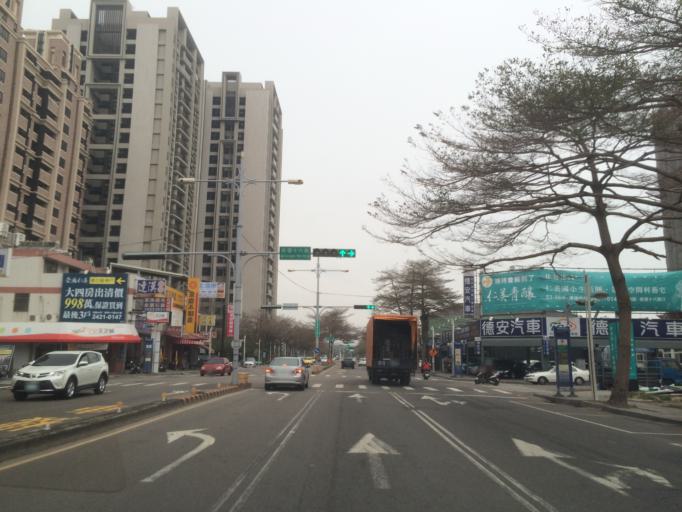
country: TW
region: Taiwan
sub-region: Taichung City
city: Taichung
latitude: 24.1948
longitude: 120.6865
